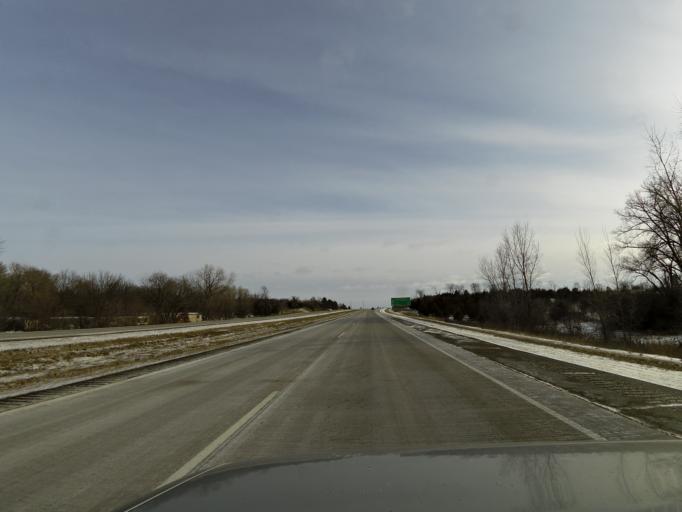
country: US
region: Wisconsin
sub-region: Pierce County
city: River Falls
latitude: 44.9190
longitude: -92.6719
